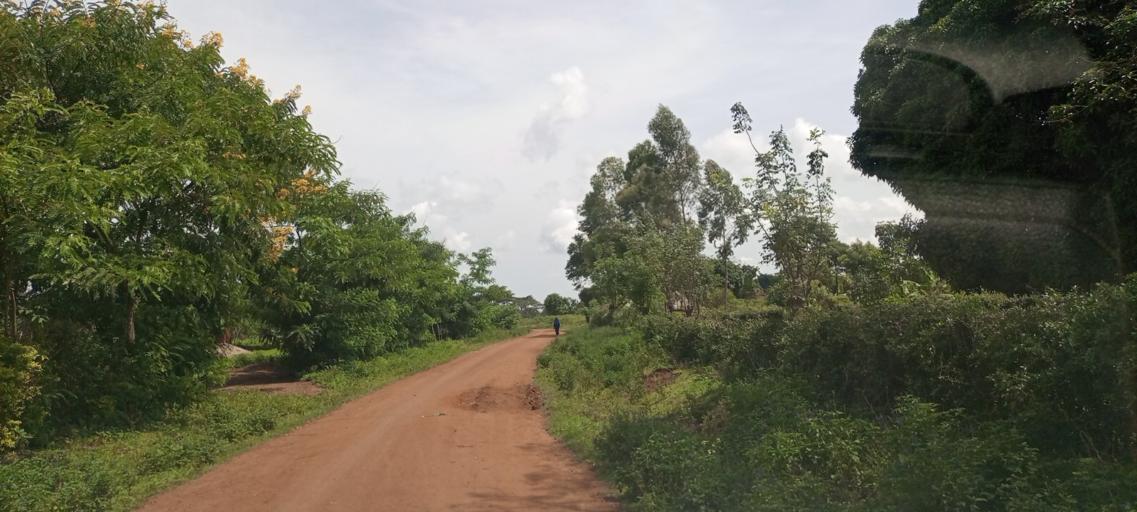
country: UG
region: Eastern Region
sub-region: Budaka District
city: Budaka
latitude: 1.1757
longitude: 33.9244
